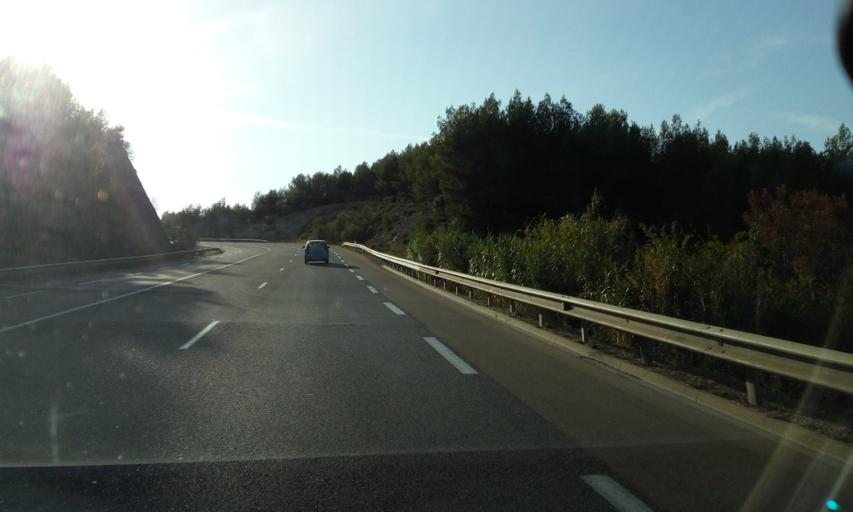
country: FR
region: Provence-Alpes-Cote d'Azur
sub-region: Departement du Var
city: Bandol
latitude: 43.1497
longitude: 5.7550
